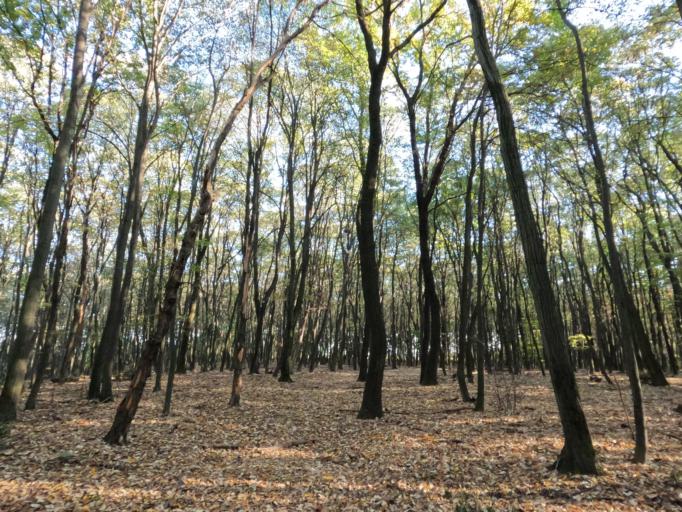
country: HU
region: Tolna
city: Szentgalpuszta
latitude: 46.3138
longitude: 18.6527
